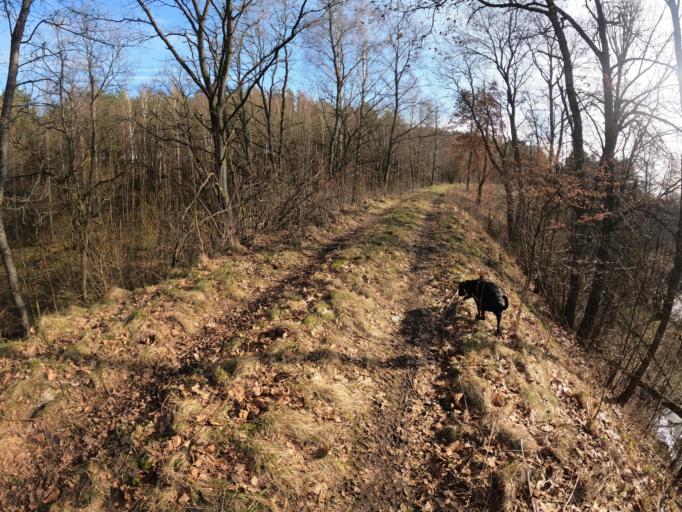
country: PL
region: West Pomeranian Voivodeship
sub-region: Powiat koszalinski
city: Bobolice
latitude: 53.9777
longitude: 16.5596
